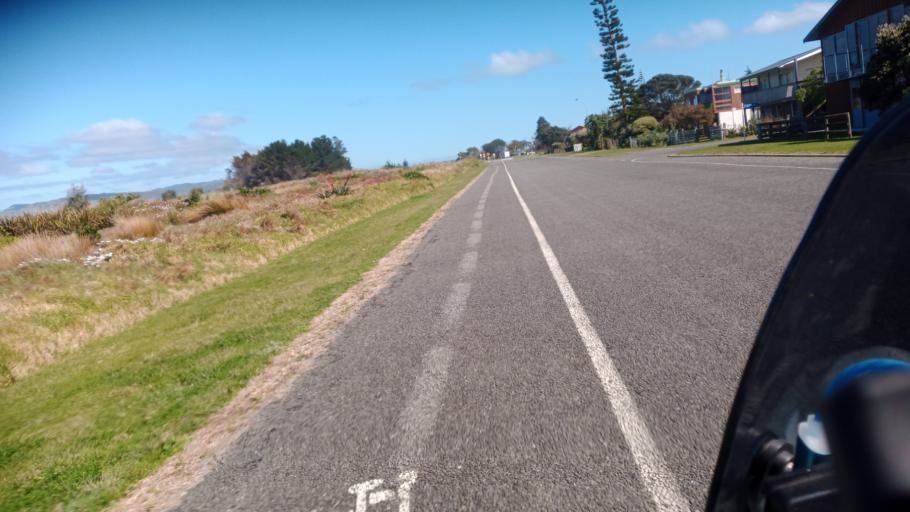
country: NZ
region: Gisborne
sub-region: Gisborne District
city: Gisborne
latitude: -39.0159
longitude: 177.8855
